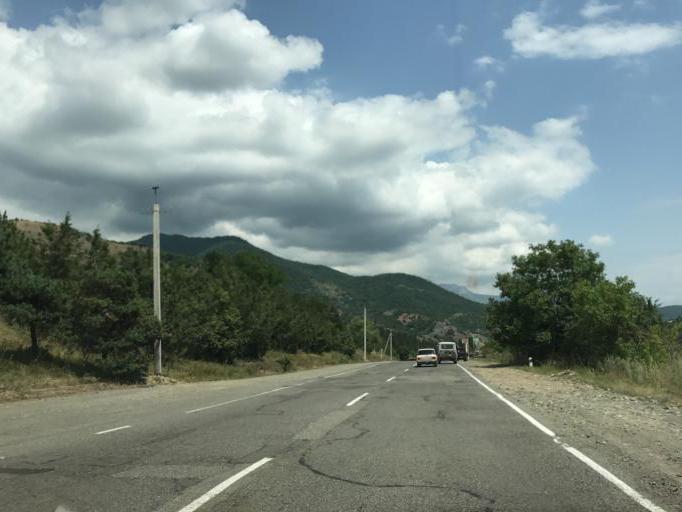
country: AM
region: Tavush
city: Dilijan
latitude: 40.7507
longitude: 44.8725
